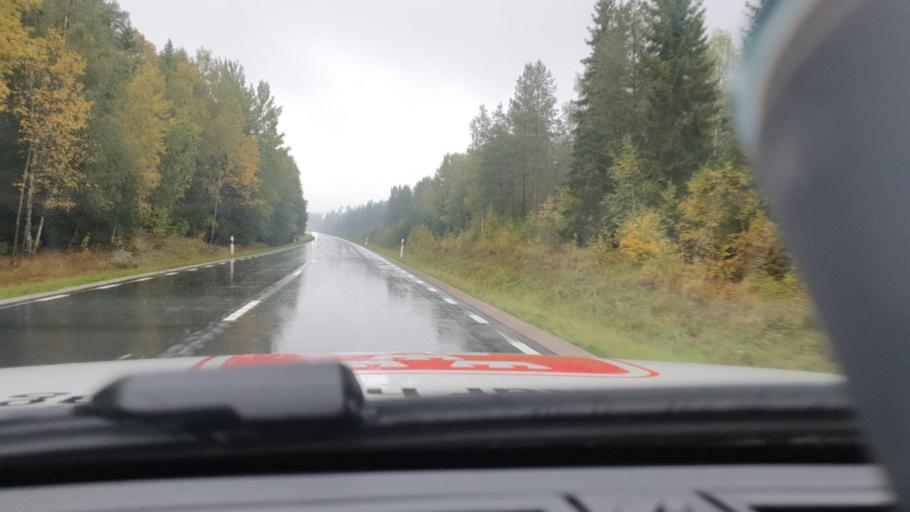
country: SE
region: Uppsala
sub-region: Tierps Kommun
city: Tierp
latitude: 60.2898
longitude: 17.5837
